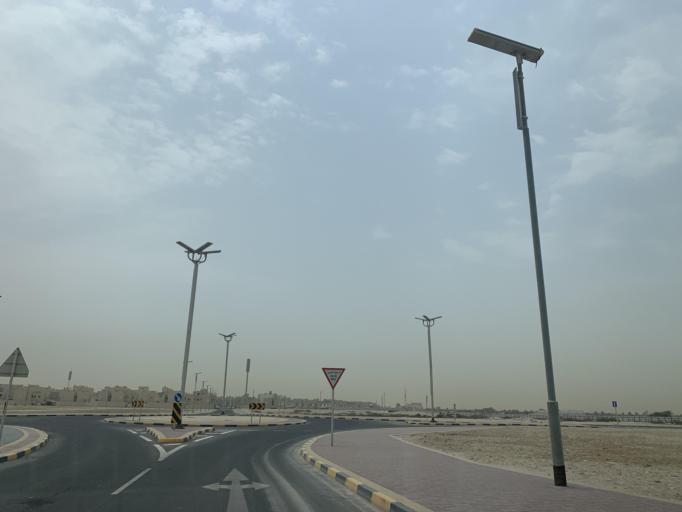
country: BH
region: Northern
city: Madinat `Isa
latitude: 26.1759
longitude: 50.5134
